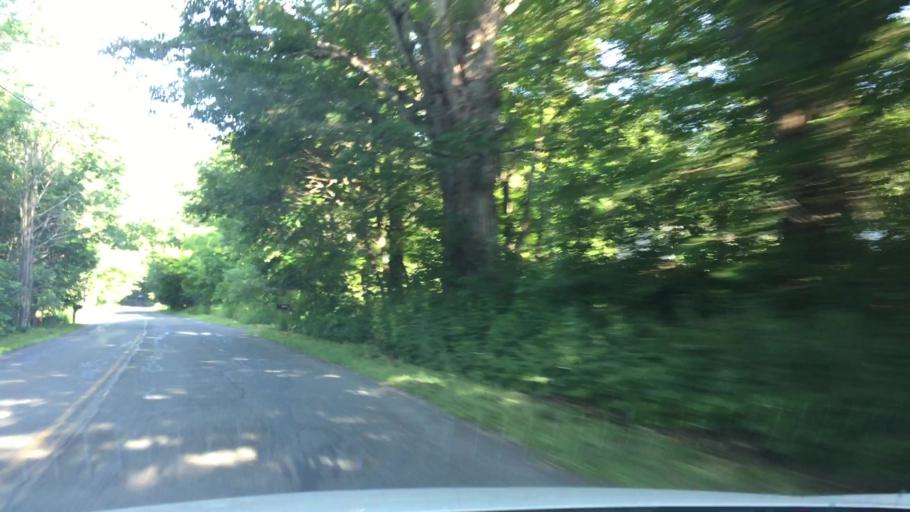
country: US
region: Massachusetts
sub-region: Berkshire County
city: Becket
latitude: 42.3172
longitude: -73.1091
